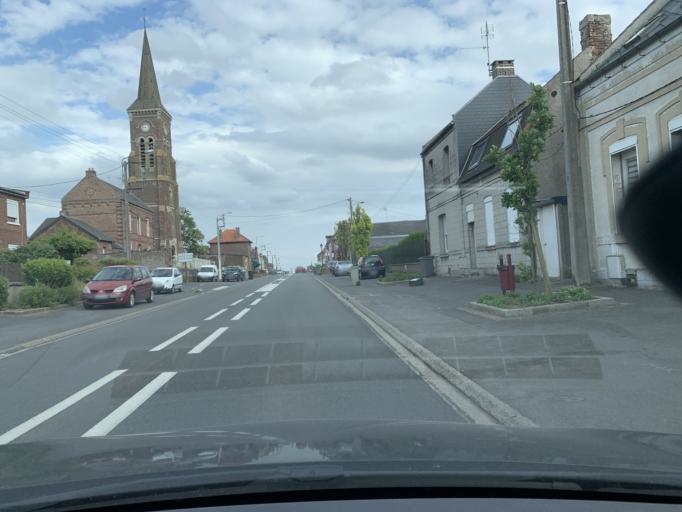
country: FR
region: Nord-Pas-de-Calais
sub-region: Departement du Nord
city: Proville
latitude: 50.1829
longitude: 3.1972
